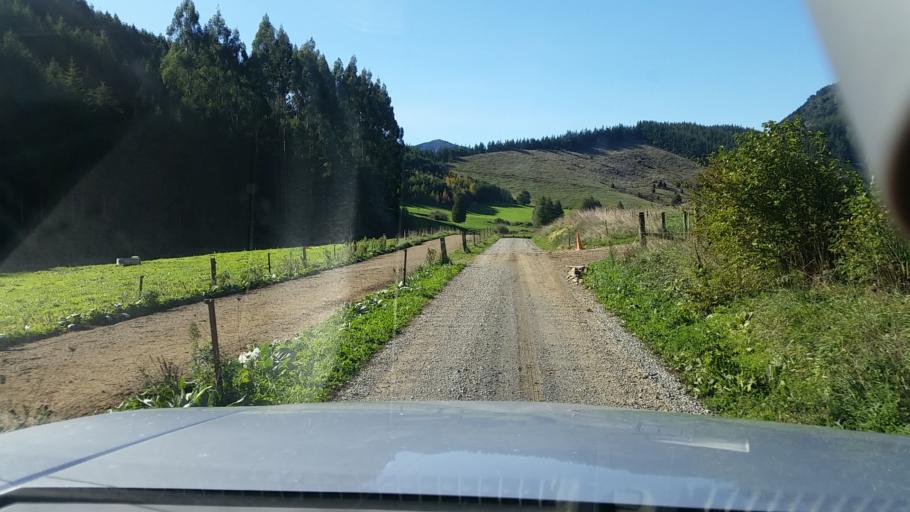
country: NZ
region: Nelson
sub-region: Nelson City
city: Nelson
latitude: -41.2226
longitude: 173.6048
